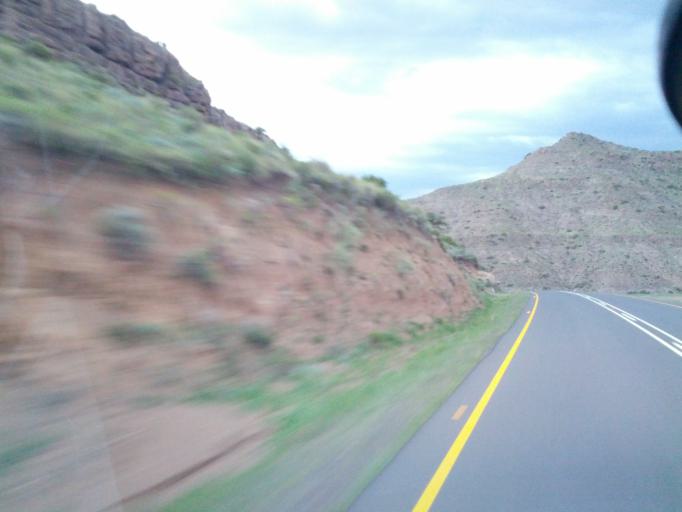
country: LS
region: Qacha's Nek
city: Qacha's Nek
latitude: -30.0402
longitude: 28.3081
